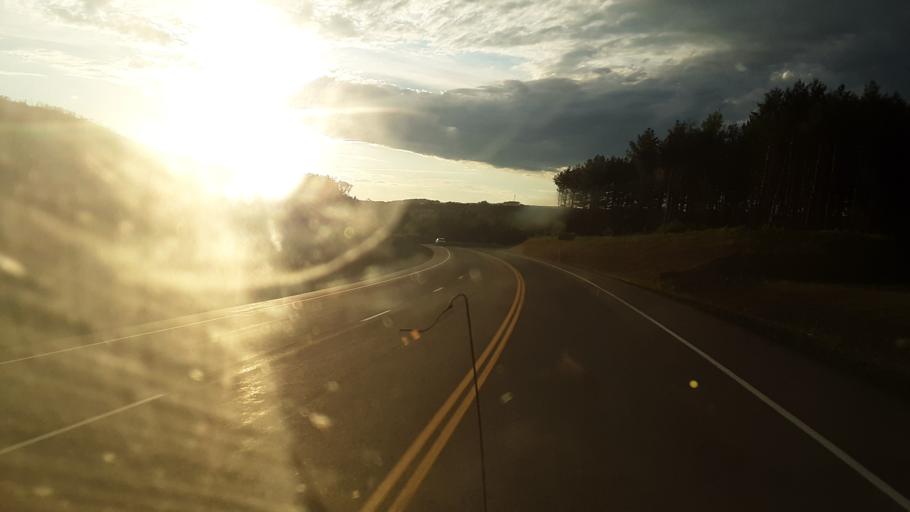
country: US
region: Maine
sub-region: Aroostook County
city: Presque Isle
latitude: 46.6924
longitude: -67.9796
